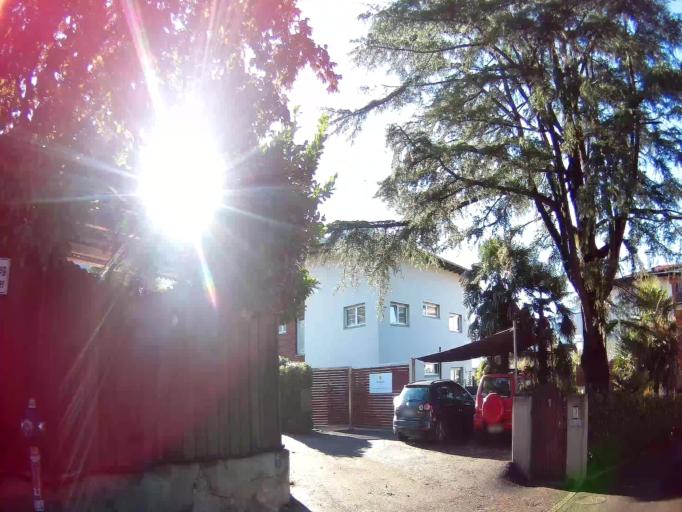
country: IT
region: Trentino-Alto Adige
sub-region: Bolzano
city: Merano
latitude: 46.6610
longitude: 11.1689
